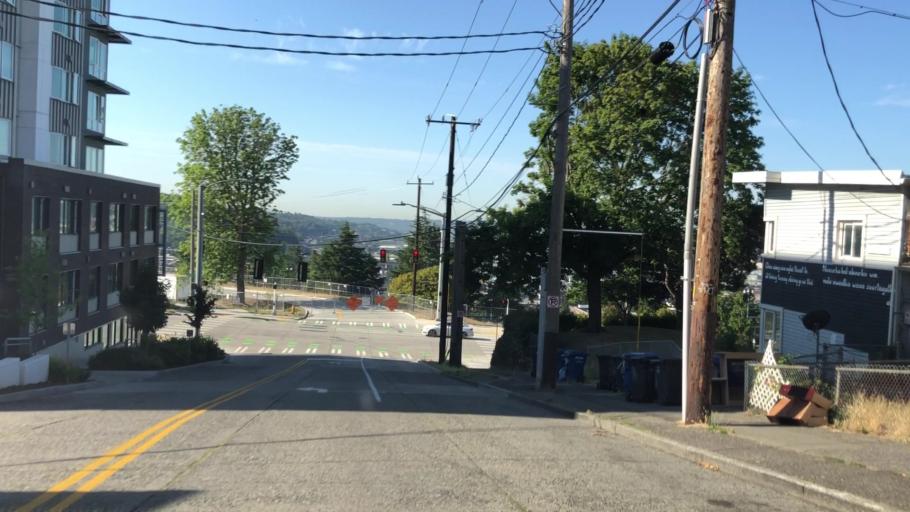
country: US
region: Washington
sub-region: King County
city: Seattle
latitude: 47.6023
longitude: -122.3225
